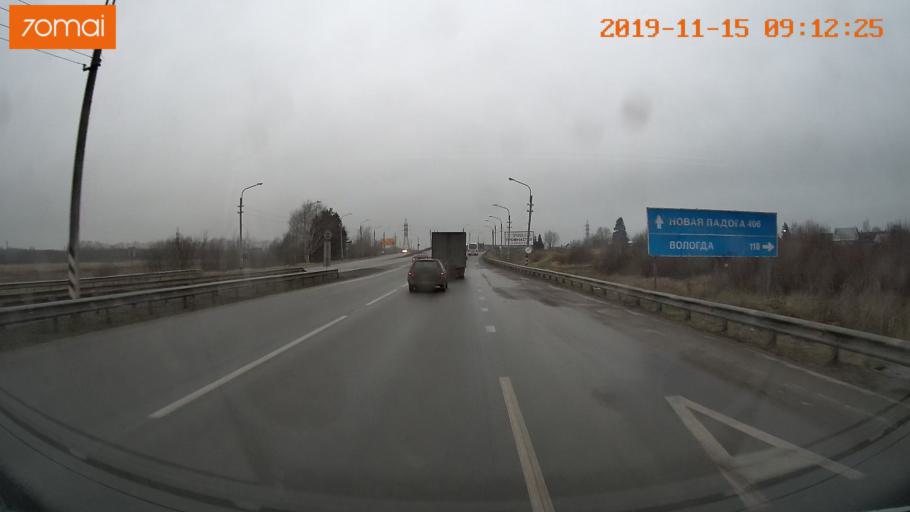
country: RU
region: Vologda
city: Tonshalovo
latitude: 59.2078
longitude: 37.9373
